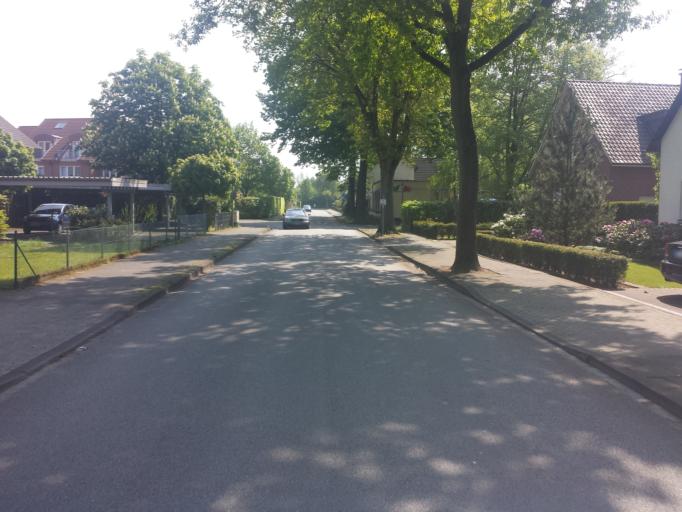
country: DE
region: North Rhine-Westphalia
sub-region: Regierungsbezirk Detmold
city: Guetersloh
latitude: 51.8892
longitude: 8.3904
